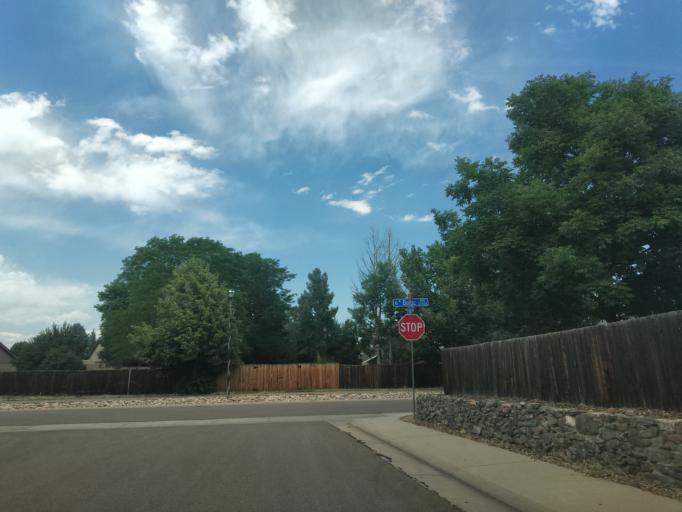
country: US
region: Colorado
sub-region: Jefferson County
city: Lakewood
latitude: 39.6760
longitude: -105.1036
